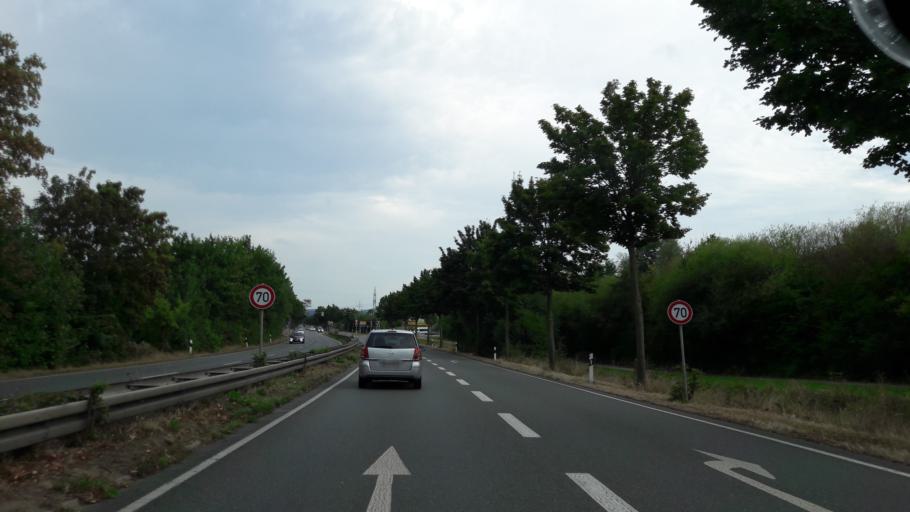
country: DE
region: Lower Saxony
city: Hildesheim
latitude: 52.1237
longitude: 9.9562
